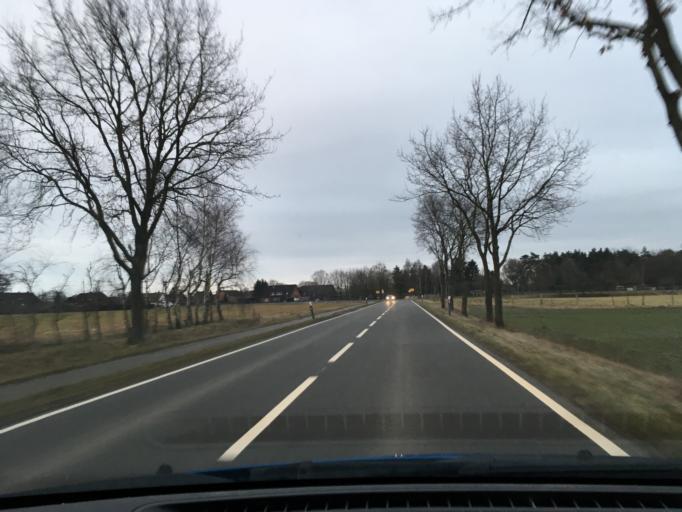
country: DE
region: Lower Saxony
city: Brietlingen
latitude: 53.3355
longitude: 10.4328
